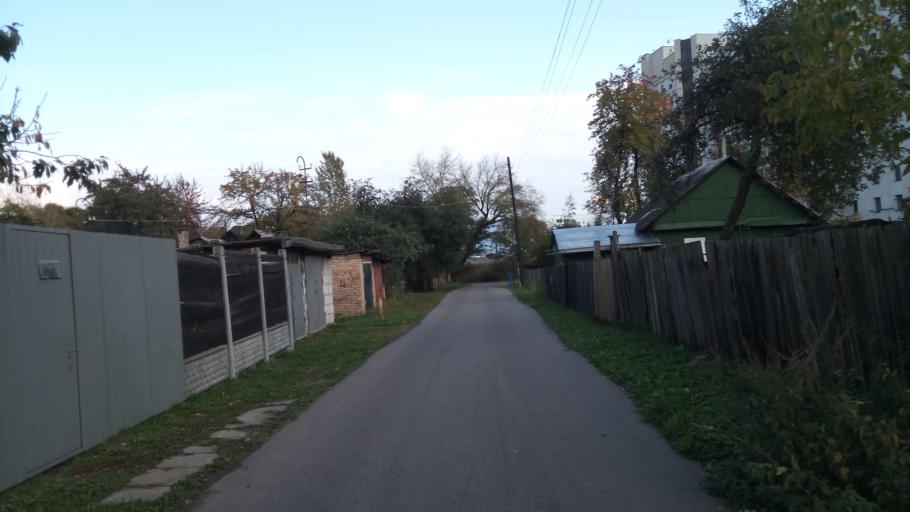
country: BY
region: Minsk
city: Minsk
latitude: 53.8870
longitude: 27.5575
